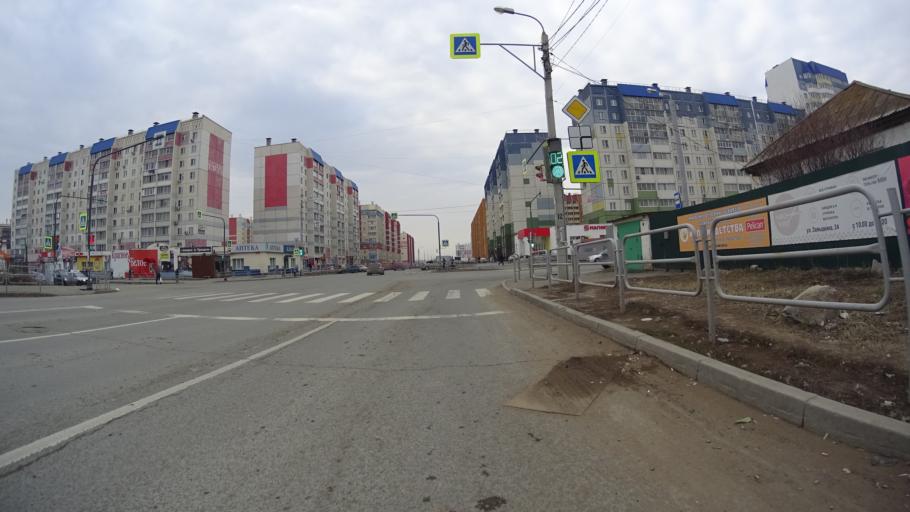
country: RU
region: Chelyabinsk
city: Zheleznodorozhnyy
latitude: 55.1666
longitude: 61.5222
